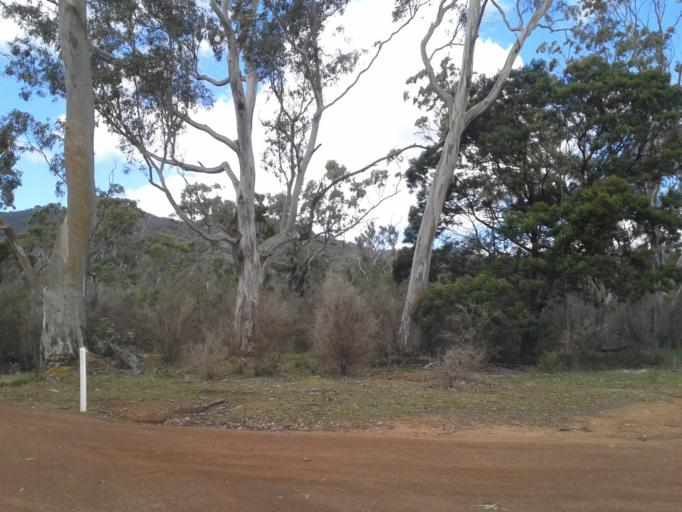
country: AU
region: Victoria
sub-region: Northern Grampians
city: Stawell
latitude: -37.2560
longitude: 142.2737
